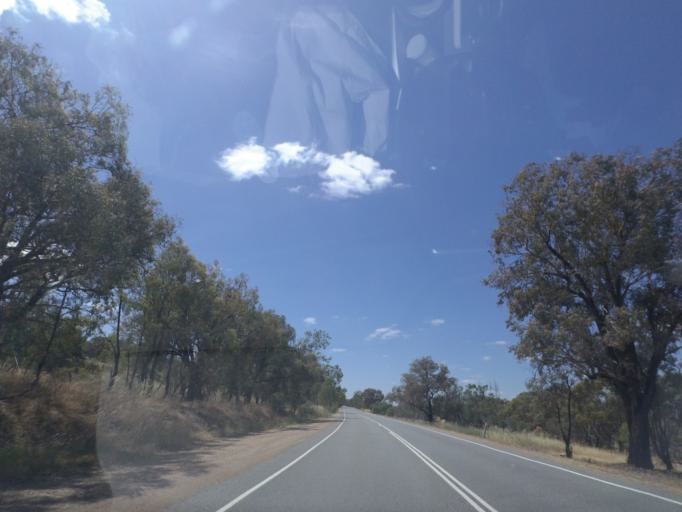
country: AU
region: Victoria
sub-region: Wangaratta
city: Wangaratta
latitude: -36.4570
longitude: 146.2365
